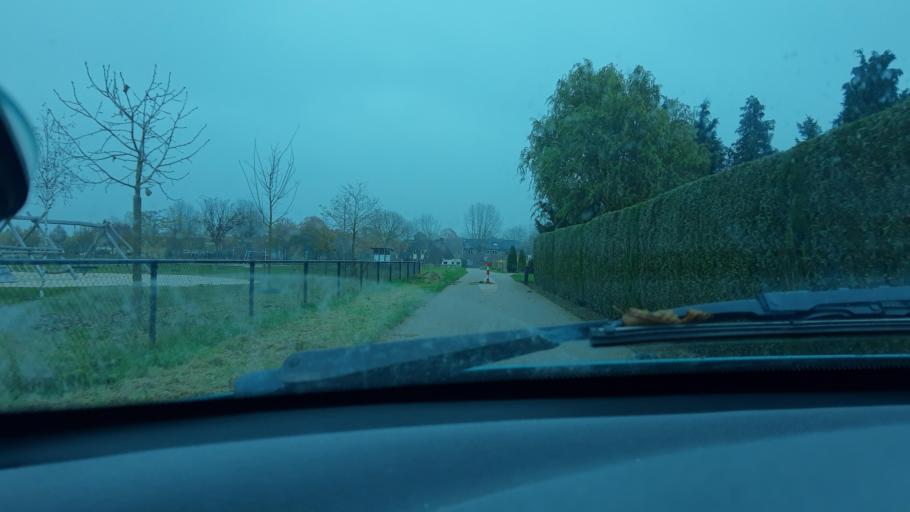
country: NL
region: North Brabant
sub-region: Gemeente Cuijk
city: Cuijk
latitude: 51.7363
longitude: 5.8546
